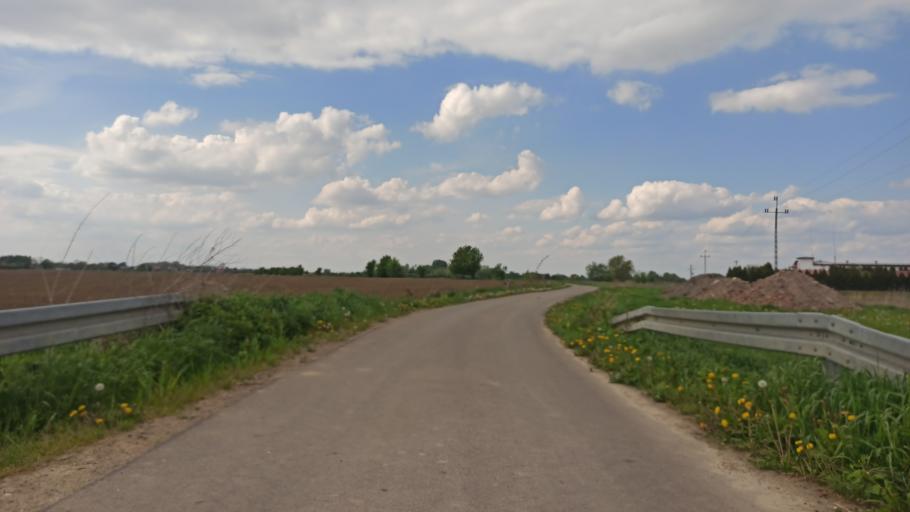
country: PL
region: Subcarpathian Voivodeship
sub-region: Powiat jaroslawski
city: Radymno
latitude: 49.9598
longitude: 22.8106
